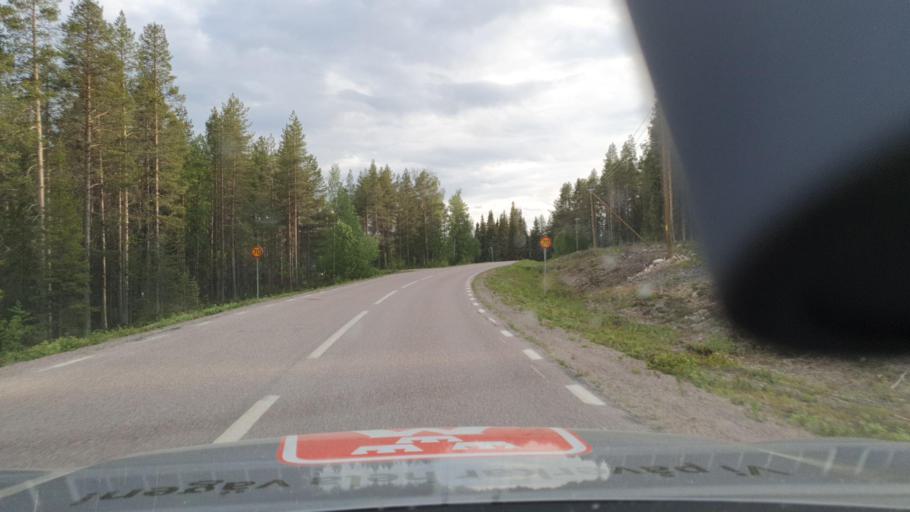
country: SE
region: Norrbotten
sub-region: Gallivare Kommun
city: Gaellivare
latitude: 66.9611
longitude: 21.2408
